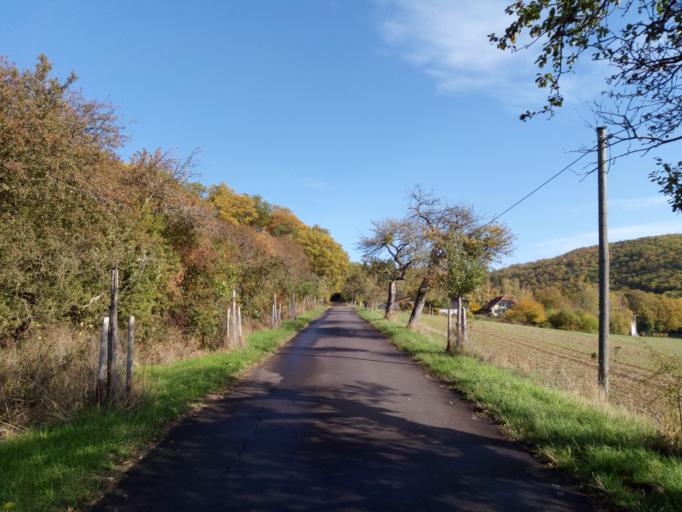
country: DE
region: Rheinland-Pfalz
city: Nussbaum
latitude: 49.8117
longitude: 7.6430
